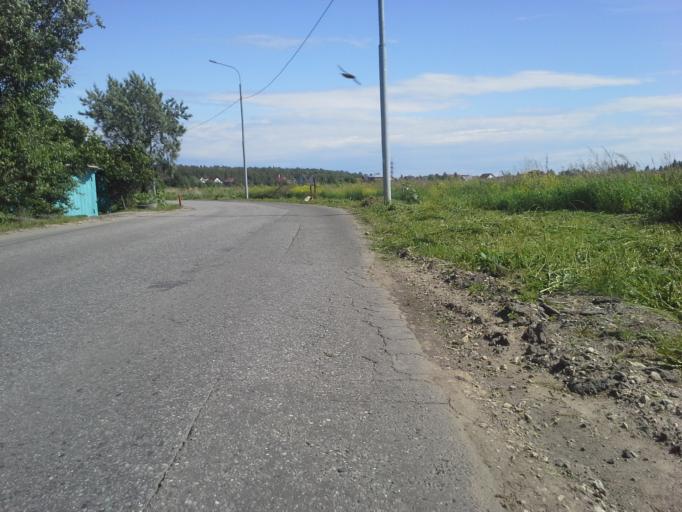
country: RU
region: Moskovskaya
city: Dubrovitsy
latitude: 55.4889
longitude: 37.4335
